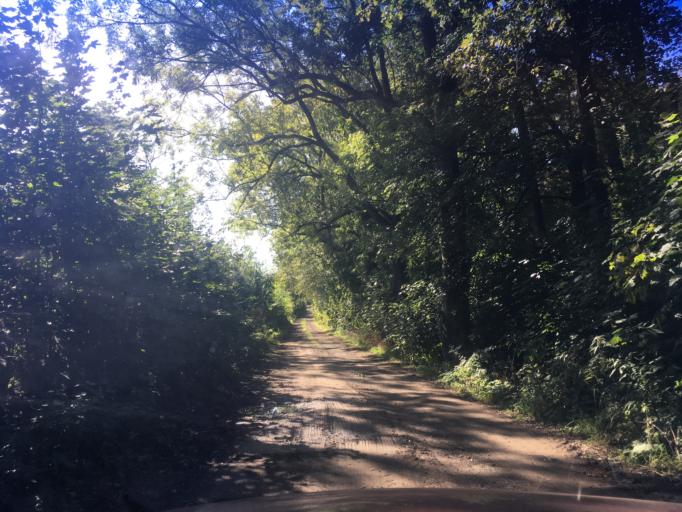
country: PL
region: Lower Silesian Voivodeship
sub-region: Powiat lubanski
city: Lesna
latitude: 51.0026
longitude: 15.1986
